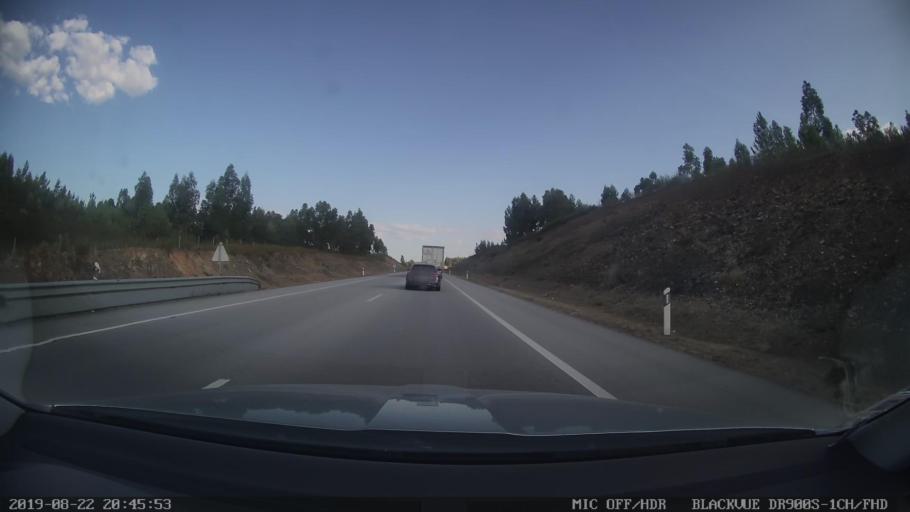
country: PT
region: Castelo Branco
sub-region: Proenca-A-Nova
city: Proenca-a-Nova
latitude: 39.7214
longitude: -7.8710
